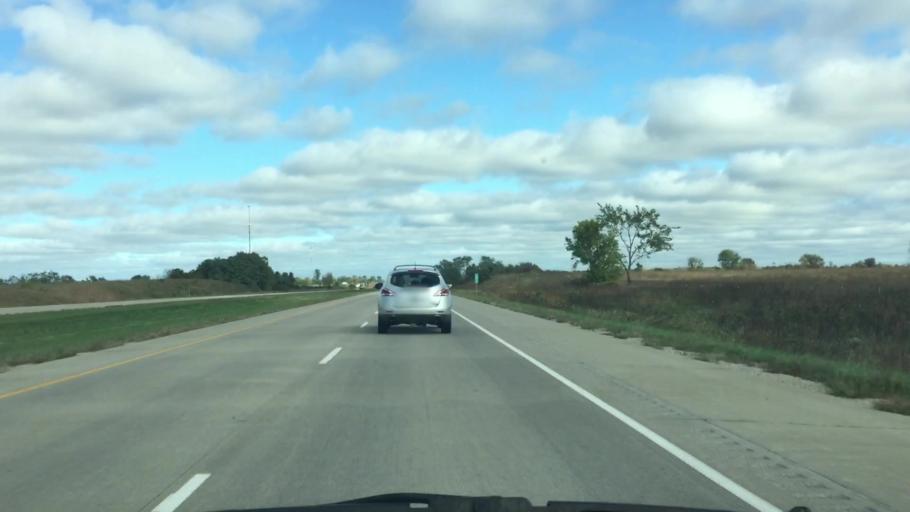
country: US
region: Iowa
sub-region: Decatur County
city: Leon
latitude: 40.8511
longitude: -93.8037
